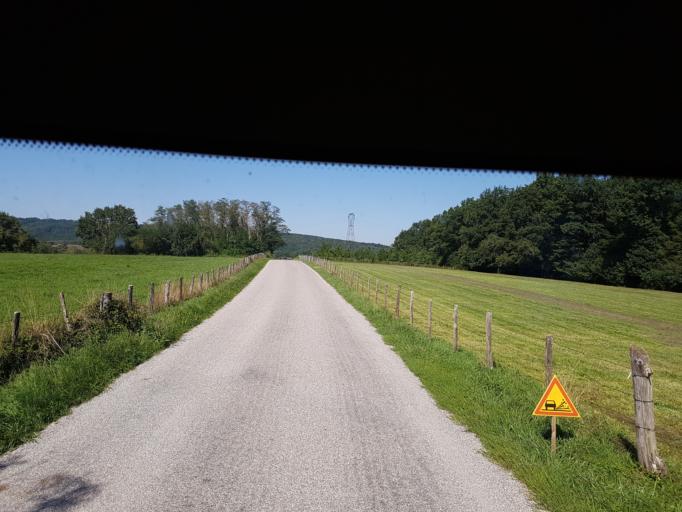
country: FR
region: Franche-Comte
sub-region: Departement du Jura
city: Perrigny
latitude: 46.7328
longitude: 5.5715
